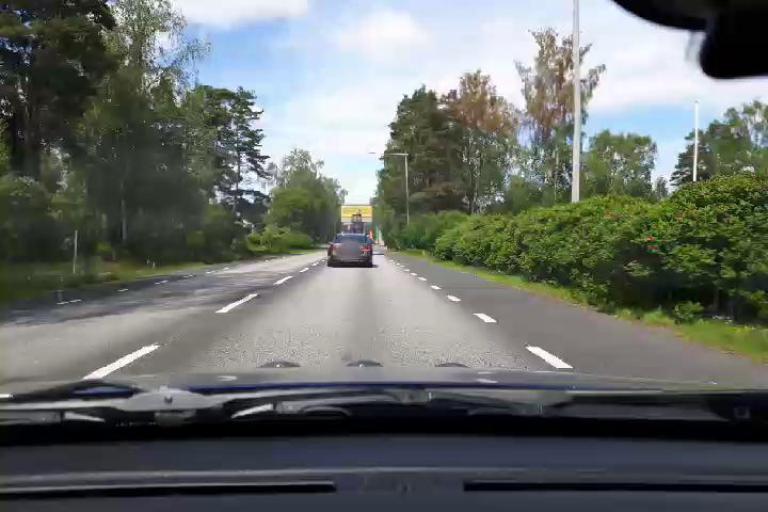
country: SE
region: Uppsala
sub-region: Osthammars Kommun
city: Bjorklinge
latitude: 60.0349
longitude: 17.5518
